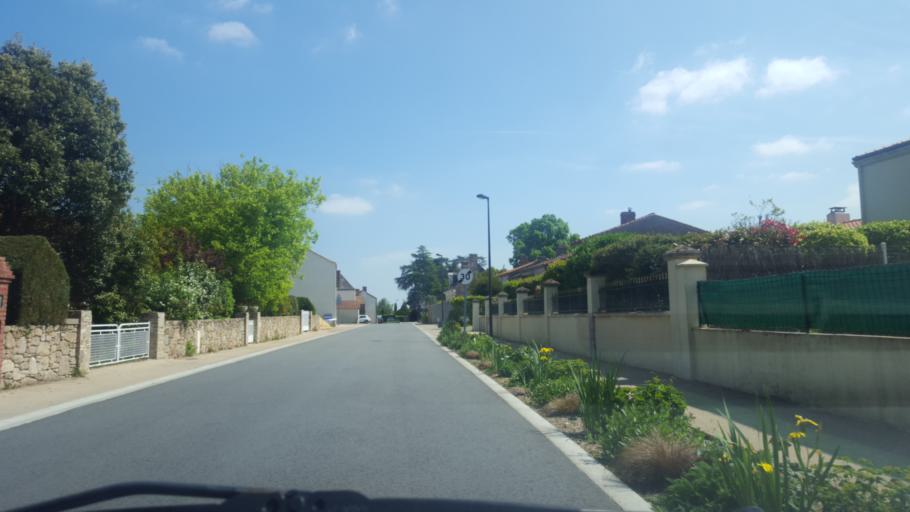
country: FR
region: Pays de la Loire
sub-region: Departement de la Loire-Atlantique
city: La Limouziniere
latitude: 46.9624
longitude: -1.5747
